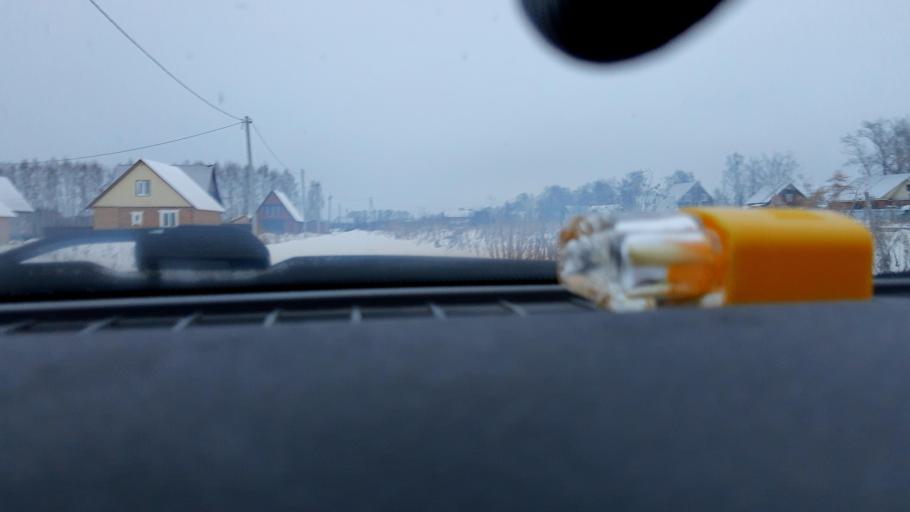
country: RU
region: Bashkortostan
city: Iglino
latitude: 54.7994
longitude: 56.4267
